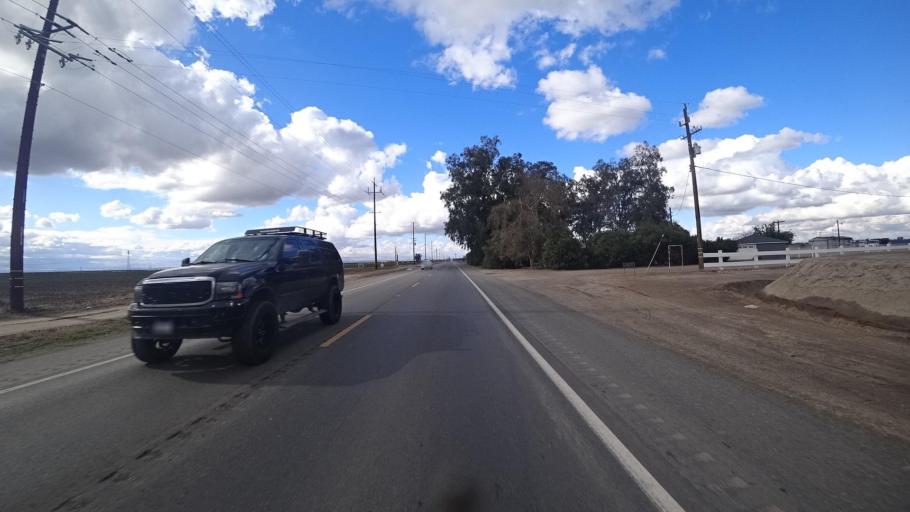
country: US
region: California
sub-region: Kern County
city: Greenfield
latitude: 35.2087
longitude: -119.0643
